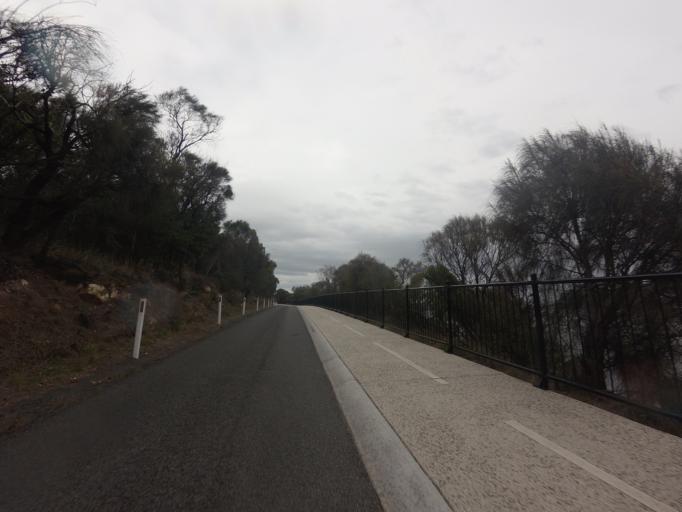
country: AU
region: Tasmania
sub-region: Clarence
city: Bellerive
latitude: -42.8818
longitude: 147.3659
